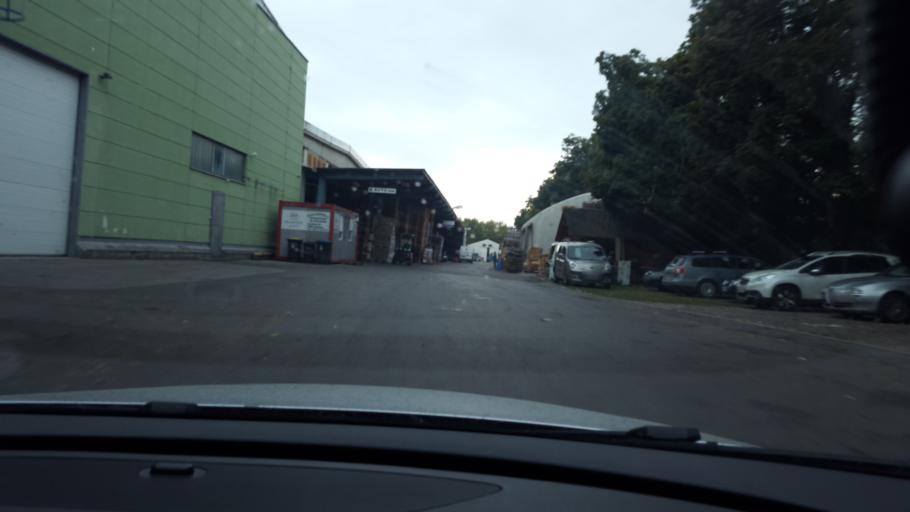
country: SI
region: Dol pri Ljubljani
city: Dol pri Ljubljani
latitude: 46.0641
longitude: 14.5644
